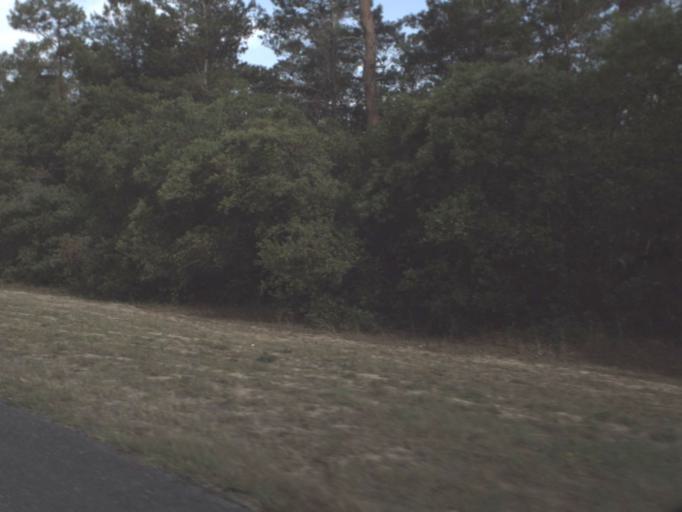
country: US
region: Florida
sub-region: Marion County
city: Silver Springs Shores
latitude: 29.1764
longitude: -81.8229
